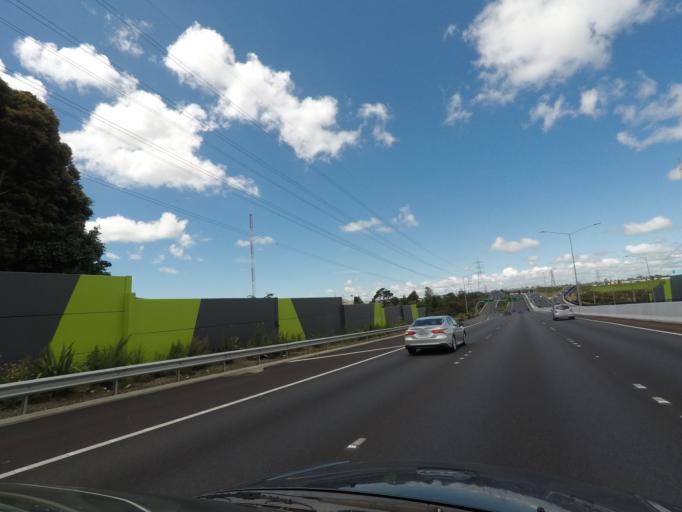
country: NZ
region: Auckland
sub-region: Auckland
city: Rosebank
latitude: -36.8443
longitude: 174.6266
